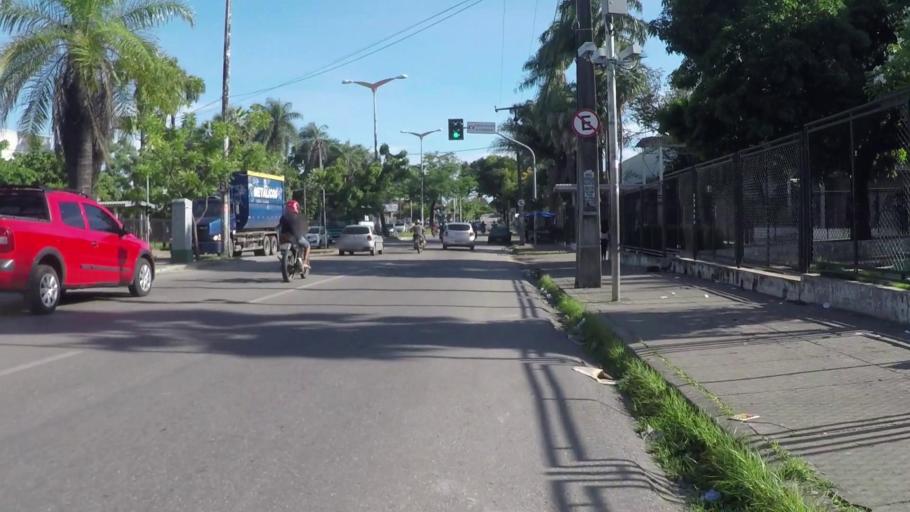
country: BR
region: Ceara
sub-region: Fortaleza
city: Fortaleza
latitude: -3.7332
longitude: -38.5843
